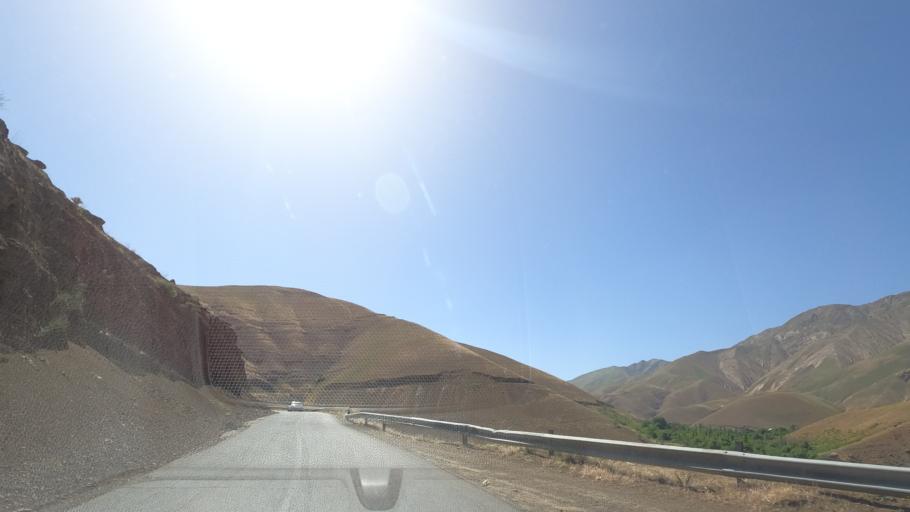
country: IR
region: Alborz
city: Karaj
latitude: 35.9328
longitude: 51.0822
